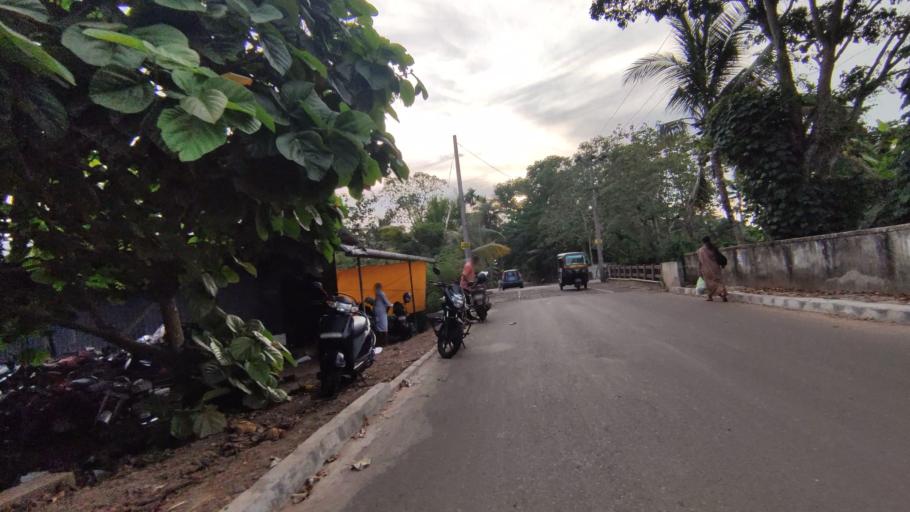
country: IN
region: Kerala
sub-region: Kottayam
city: Kottayam
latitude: 9.6435
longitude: 76.5158
